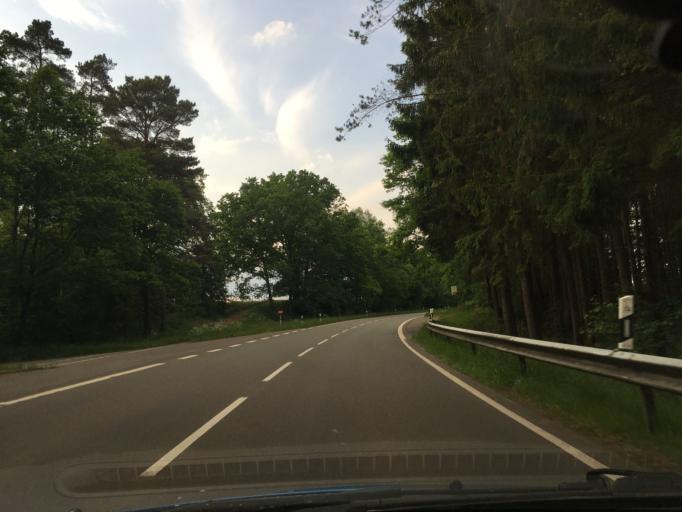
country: DE
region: Lower Saxony
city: Oldendorf
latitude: 53.1432
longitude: 10.2112
